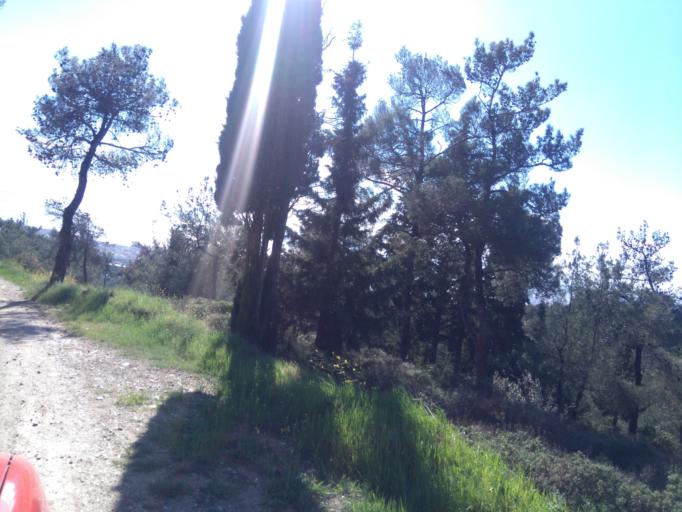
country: GR
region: Central Macedonia
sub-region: Nomos Thessalonikis
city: Triandria
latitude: 40.6334
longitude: 22.9796
